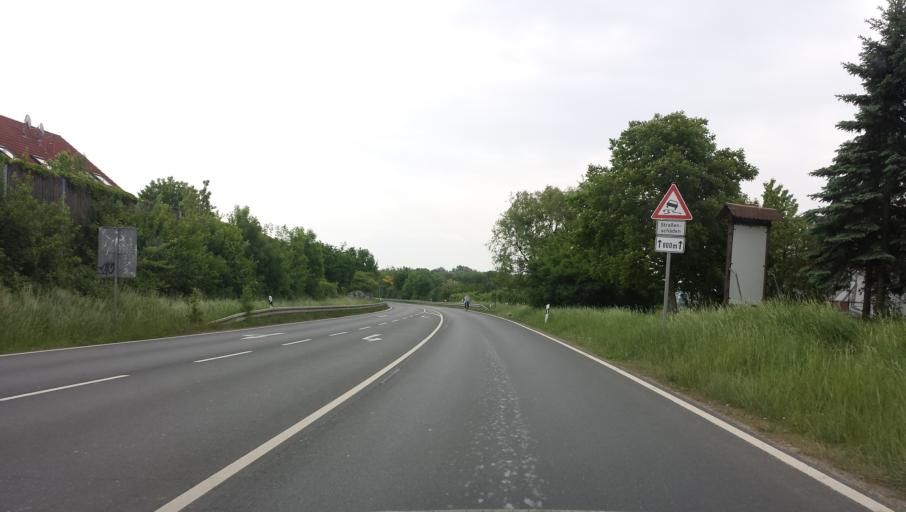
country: DE
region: Hesse
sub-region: Regierungsbezirk Darmstadt
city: Bad Vilbel
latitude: 50.1986
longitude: 8.7082
